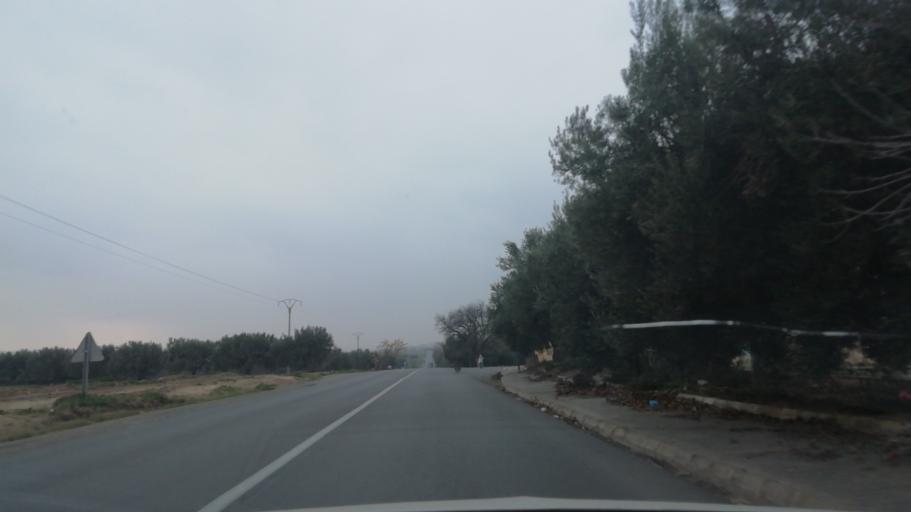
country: DZ
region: Sidi Bel Abbes
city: Sfizef
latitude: 35.2529
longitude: -0.1933
